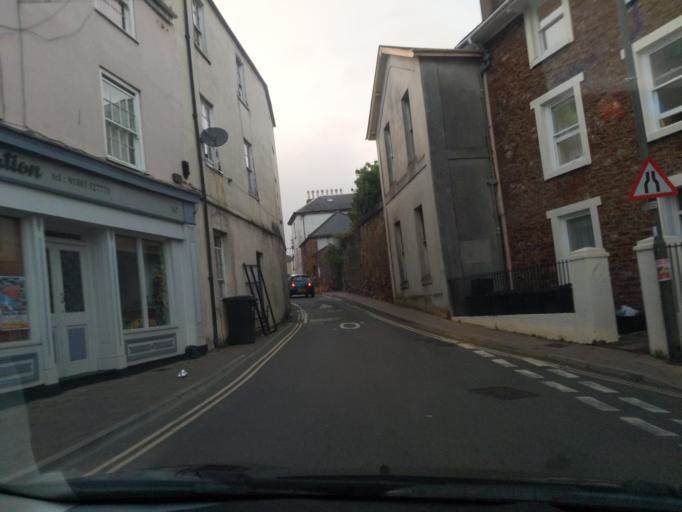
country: GB
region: England
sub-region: Borough of Torbay
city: Paignton
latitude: 50.4368
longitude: -3.5716
